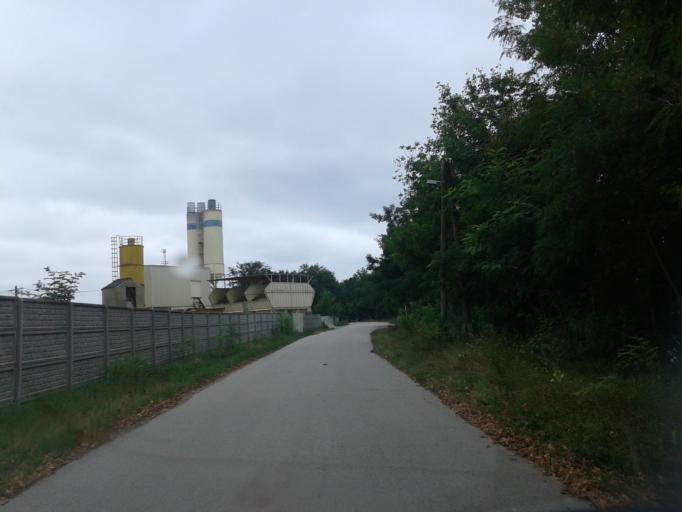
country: HU
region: Bacs-Kiskun
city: Harta
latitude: 46.6973
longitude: 19.0117
